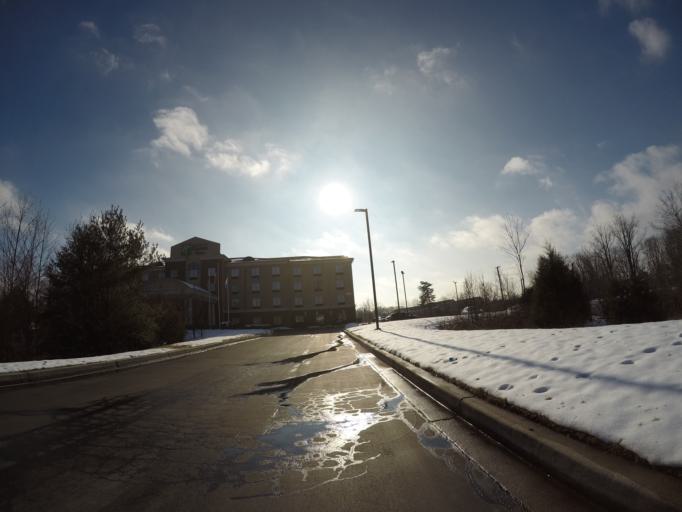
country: US
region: Maryland
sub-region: Howard County
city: Ilchester
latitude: 39.2086
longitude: -76.7785
